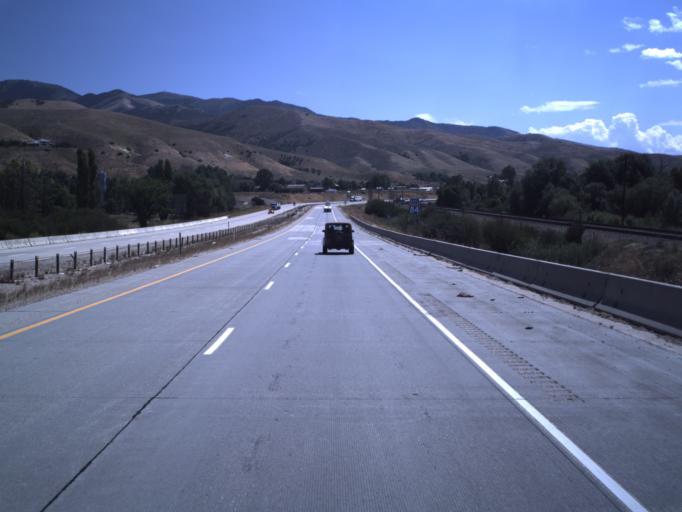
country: US
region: Utah
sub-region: Morgan County
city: Mountain Green
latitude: 41.1121
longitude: -111.7591
